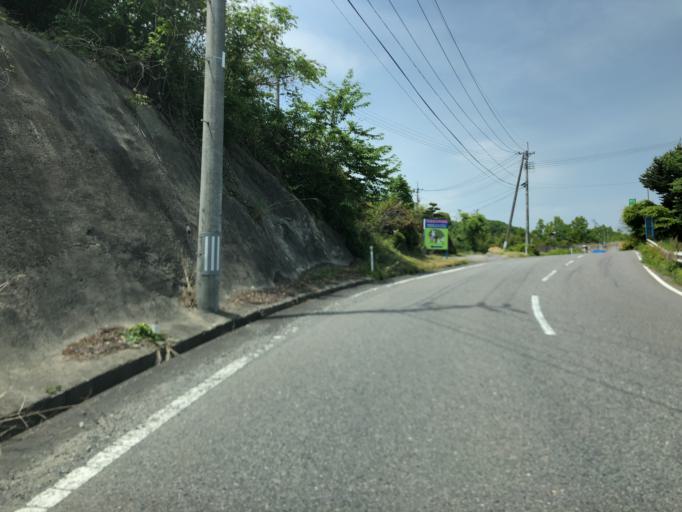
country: JP
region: Fukushima
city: Ishikawa
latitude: 37.1914
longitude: 140.4835
